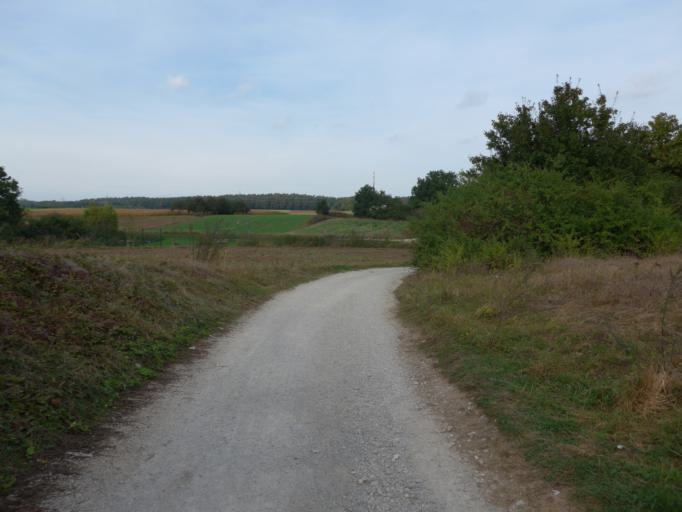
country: DE
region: Bavaria
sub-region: Regierungsbezirk Mittelfranken
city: Erlangen
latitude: 49.5481
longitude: 11.0159
